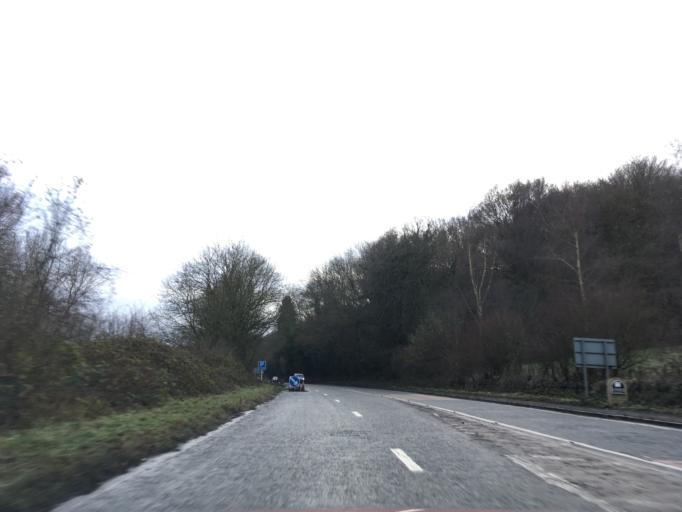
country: GB
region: England
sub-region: Gloucestershire
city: Charlton Kings
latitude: 51.8710
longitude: -2.0529
